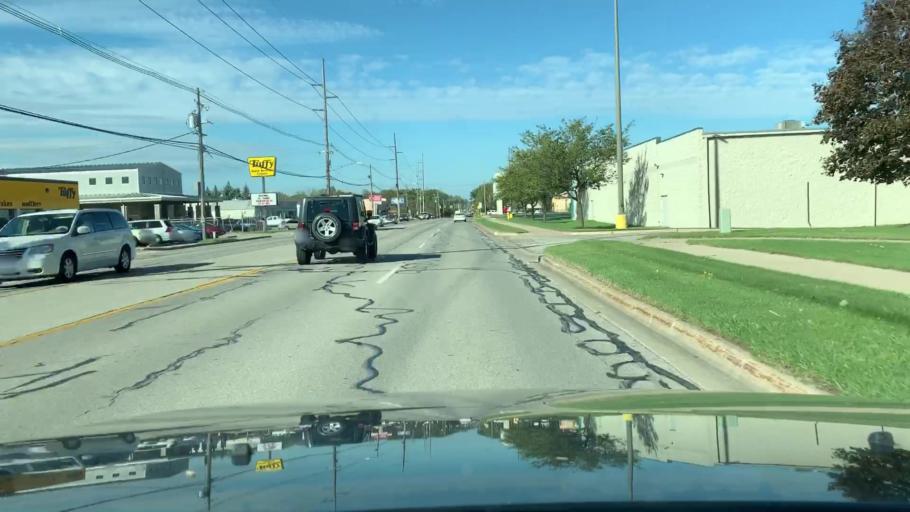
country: US
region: Michigan
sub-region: Ottawa County
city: Holland
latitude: 42.7943
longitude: -86.0777
